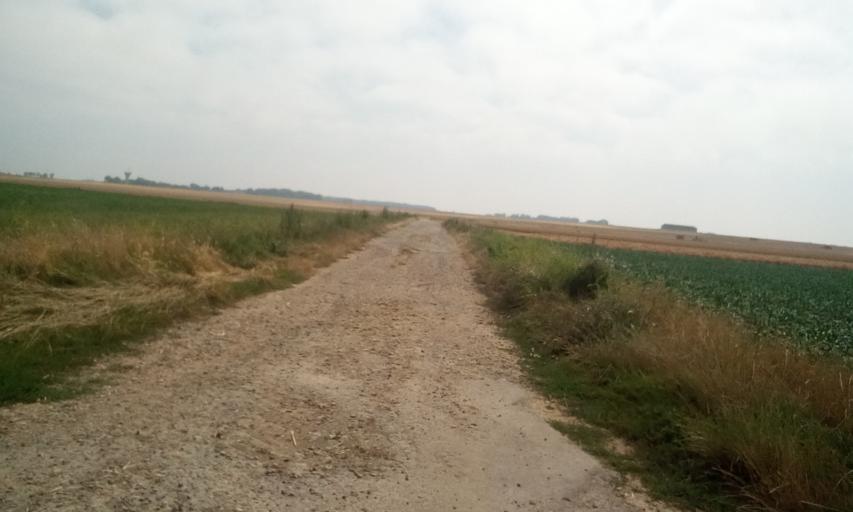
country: FR
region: Lower Normandy
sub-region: Departement du Calvados
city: Bernieres-sur-Mer
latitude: 49.3273
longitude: -0.4105
